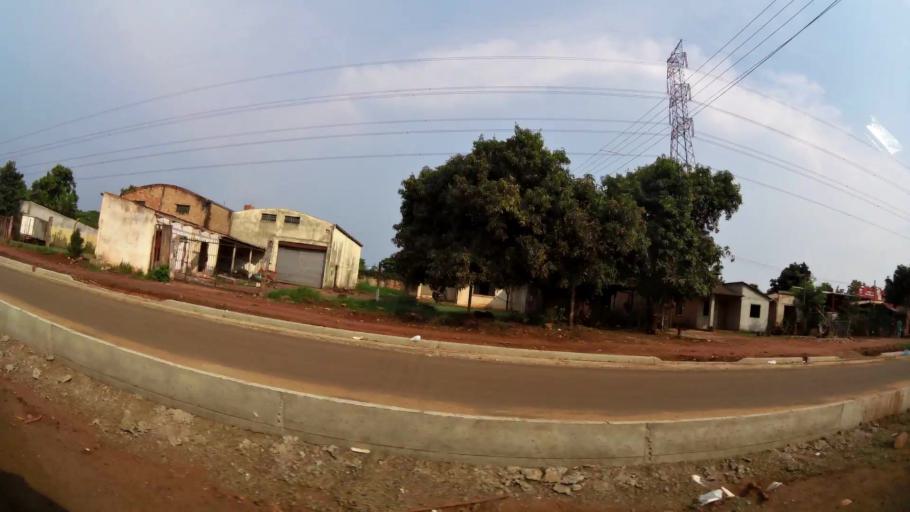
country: PY
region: Alto Parana
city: Ciudad del Este
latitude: -25.4732
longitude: -54.6478
